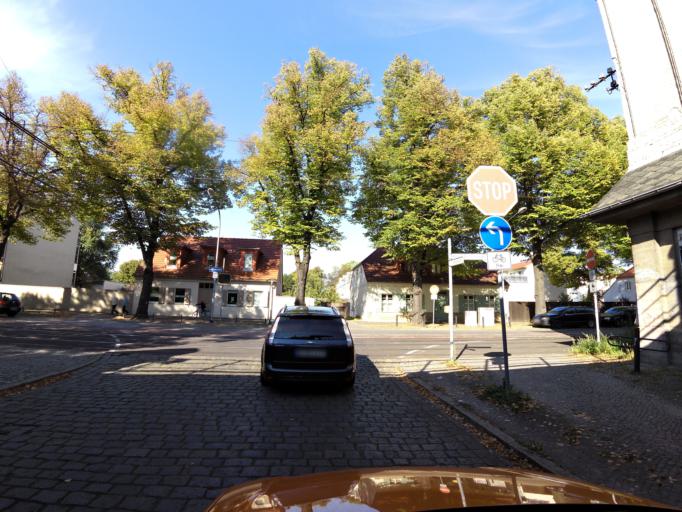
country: DE
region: Brandenburg
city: Potsdam
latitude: 52.3920
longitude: 13.1002
